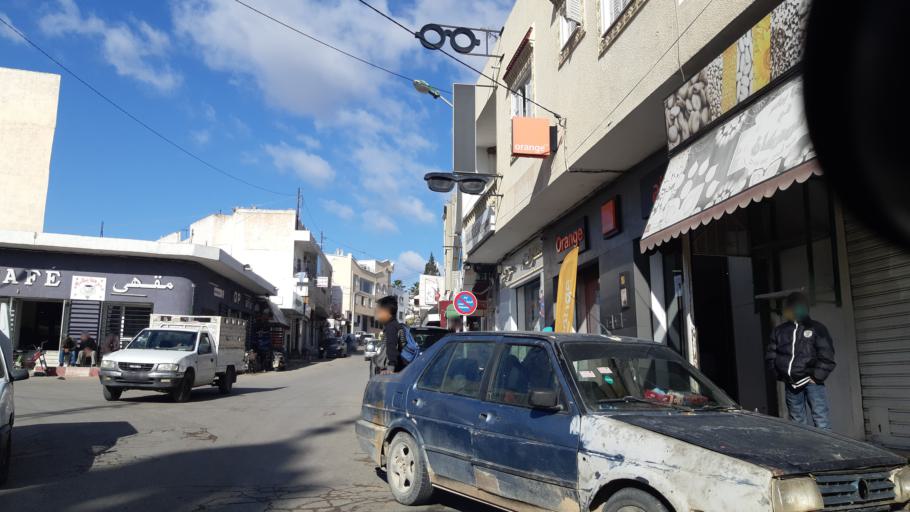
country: TN
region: Susah
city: Akouda
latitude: 35.8705
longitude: 10.5369
